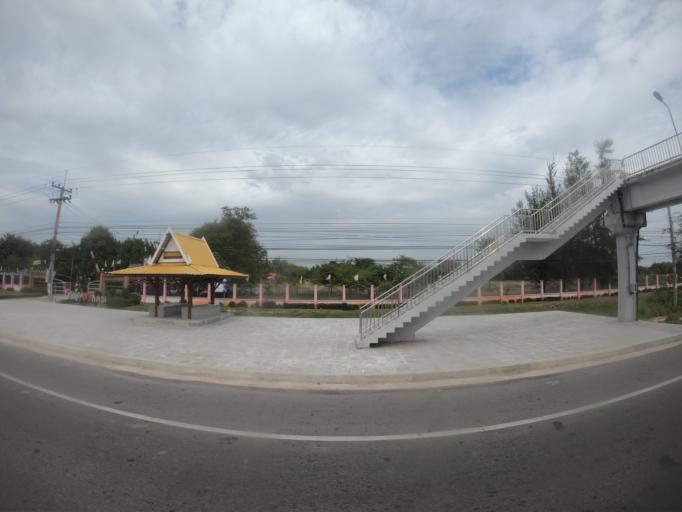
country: TH
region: Roi Et
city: Changhan
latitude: 16.0758
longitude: 103.5884
